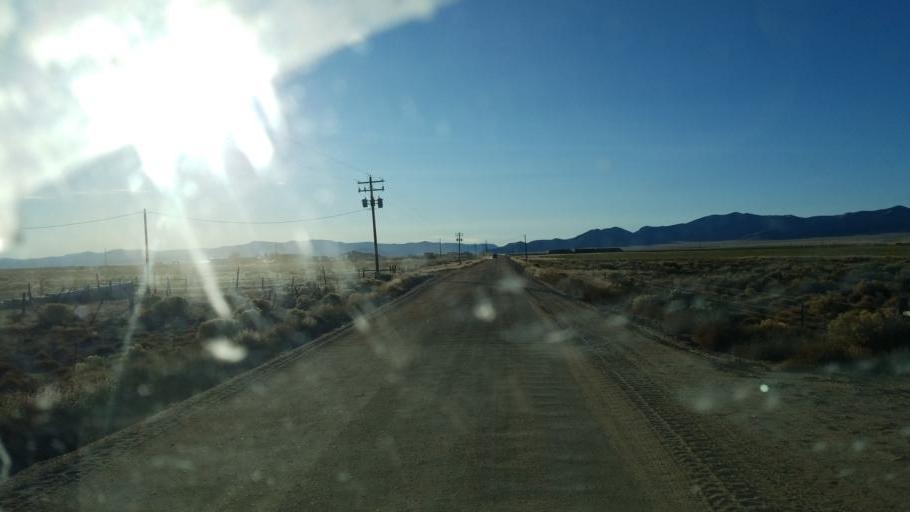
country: US
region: Colorado
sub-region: Saguache County
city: Saguache
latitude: 38.1005
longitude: -105.9115
